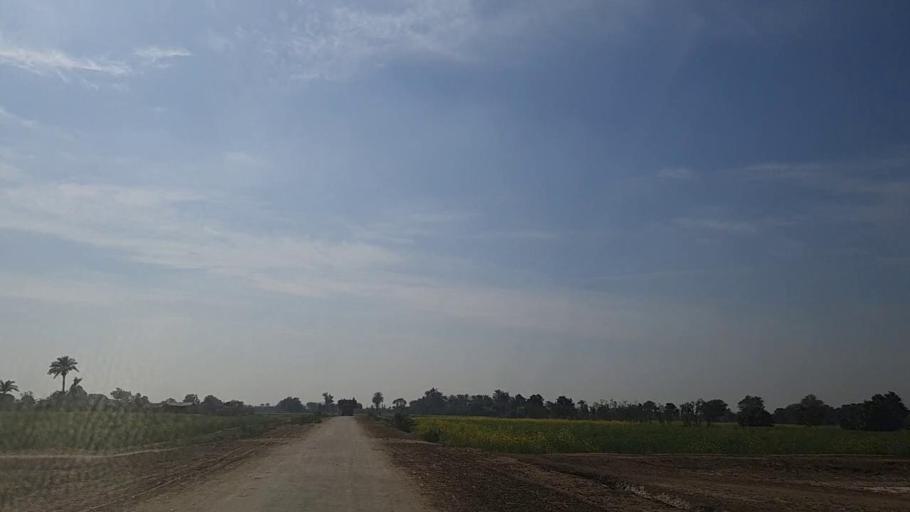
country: PK
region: Sindh
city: Mirpur Khas
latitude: 25.4720
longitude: 68.9645
